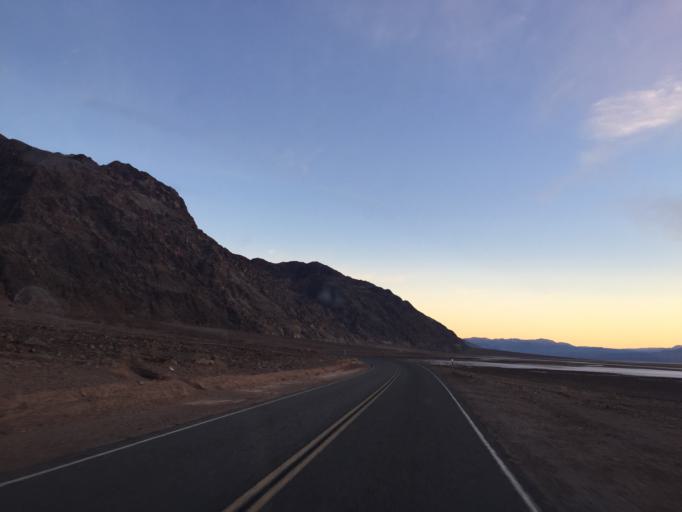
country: US
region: Nevada
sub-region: Nye County
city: Beatty
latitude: 36.1931
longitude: -116.7722
